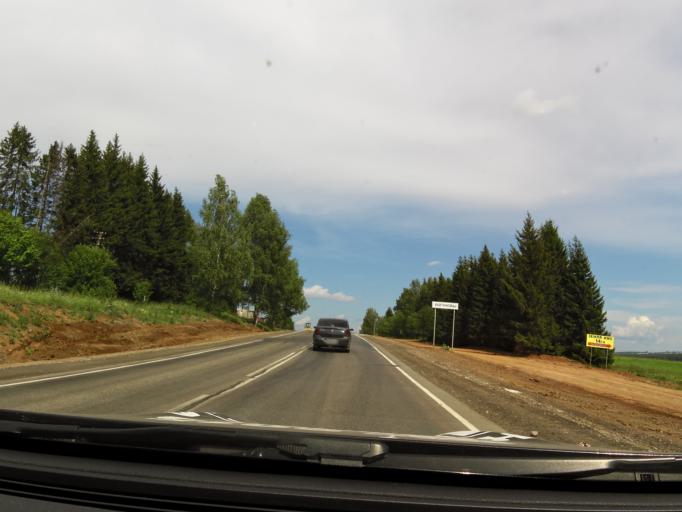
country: RU
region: Kirov
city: Vakhrushi
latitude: 58.6759
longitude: 49.9641
